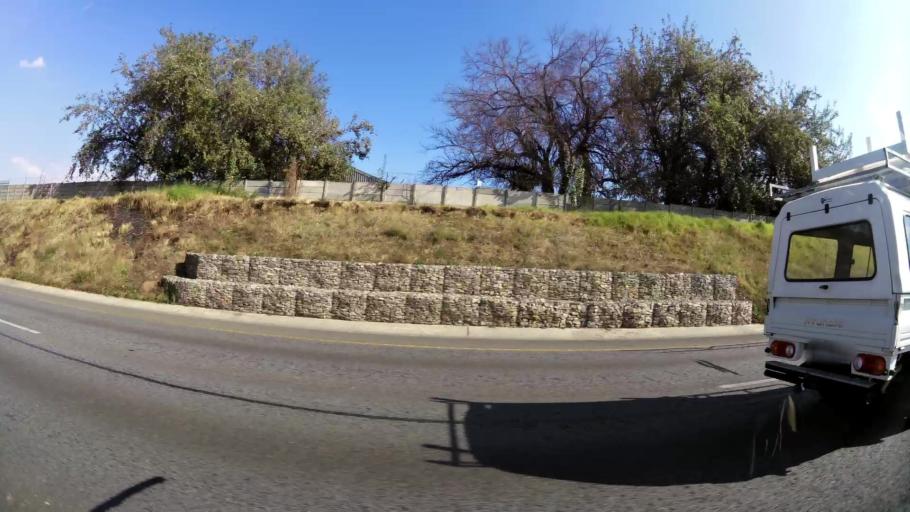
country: ZA
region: Gauteng
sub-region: Ekurhuleni Metropolitan Municipality
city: Tembisa
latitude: -26.0795
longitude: 28.2717
